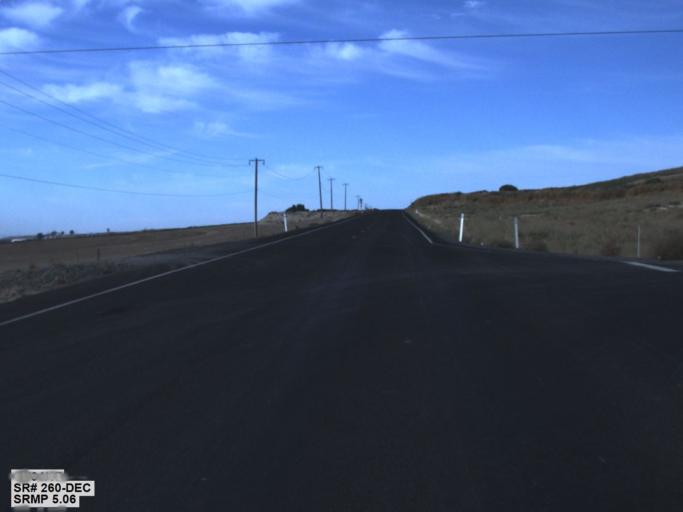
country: US
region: Washington
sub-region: Franklin County
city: Connell
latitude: 46.6634
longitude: -118.8999
